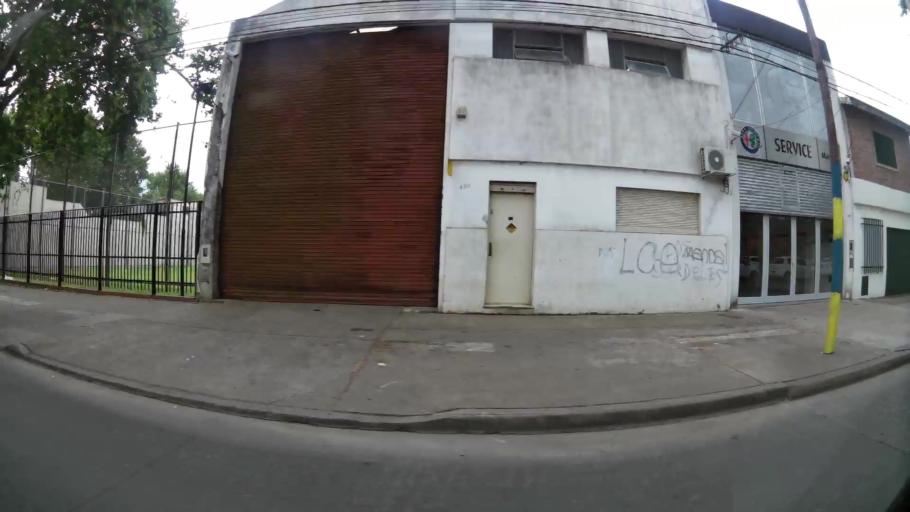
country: AR
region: Santa Fe
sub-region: Departamento de Rosario
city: Rosario
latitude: -32.9264
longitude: -60.6701
